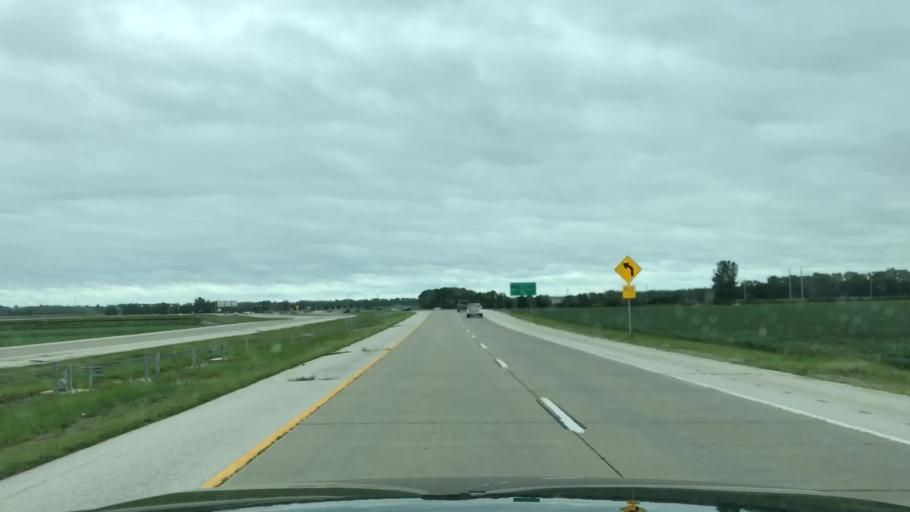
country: US
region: Missouri
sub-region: Saint Charles County
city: Saint Charles
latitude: 38.7191
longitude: -90.4984
